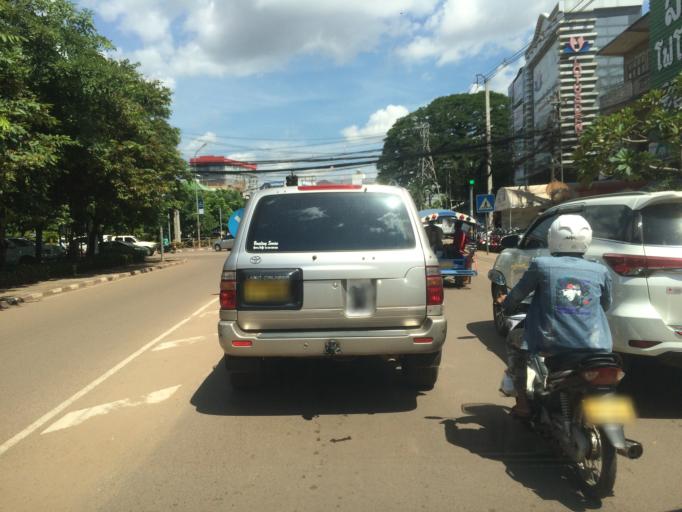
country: LA
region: Vientiane
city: Vientiane
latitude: 17.9681
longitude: 102.6118
